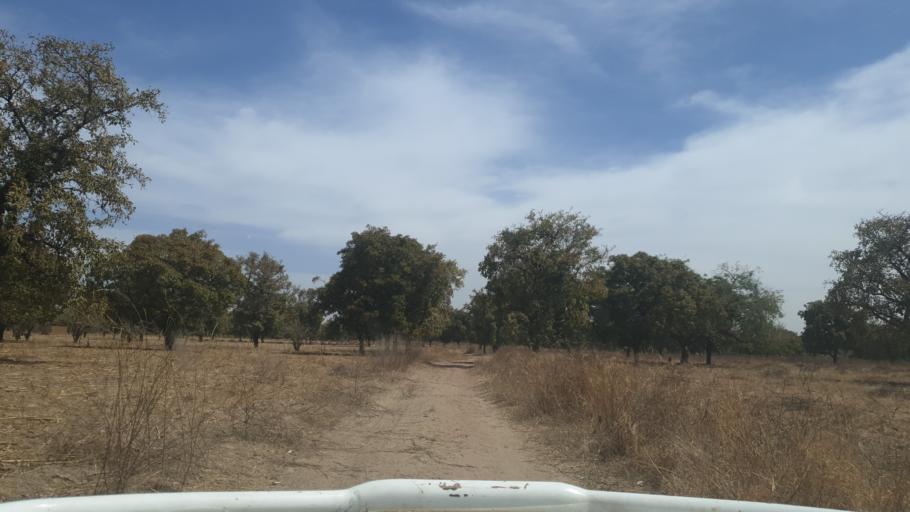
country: ML
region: Sikasso
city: Yorosso
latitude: 12.2878
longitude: -4.6740
